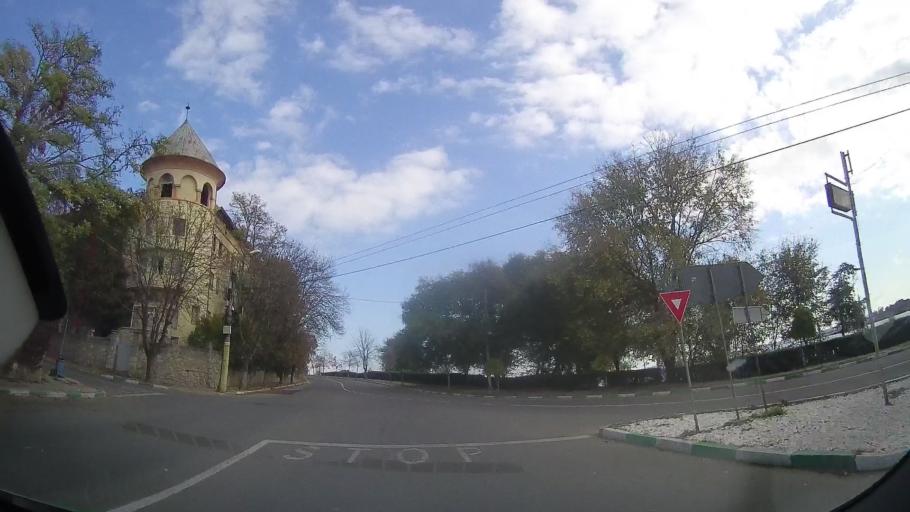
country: RO
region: Constanta
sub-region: Oras Techirghiol
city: Techirghiol
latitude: 44.0550
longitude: 28.6033
